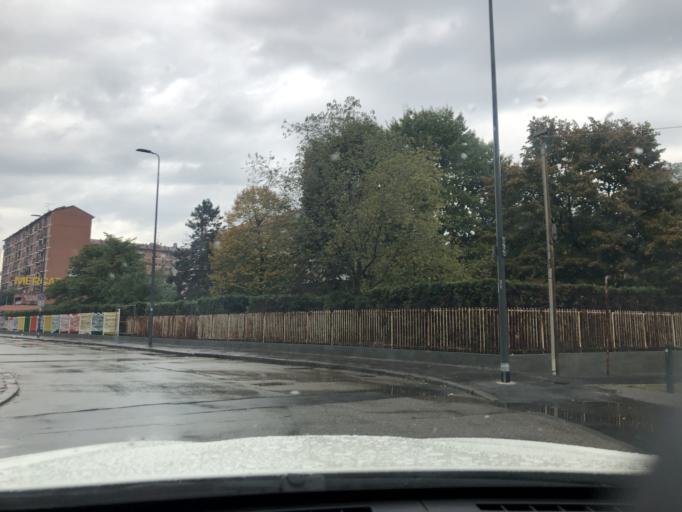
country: IT
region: Lombardy
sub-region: Citta metropolitana di Milano
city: Baranzate
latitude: 45.4901
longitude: 9.1229
